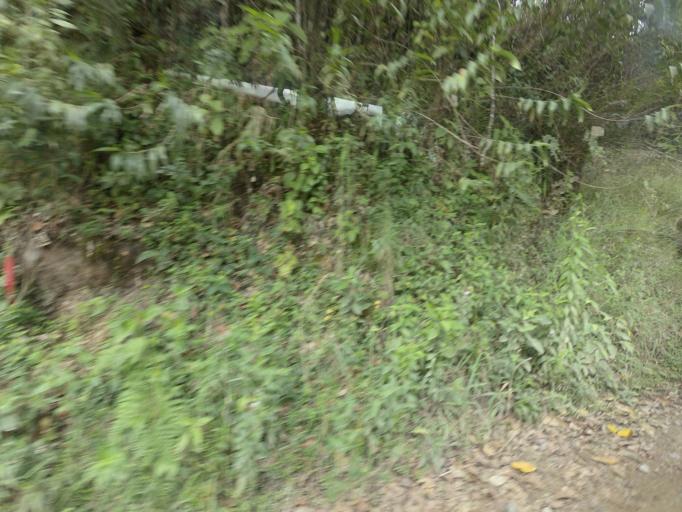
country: CO
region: Huila
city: San Agustin
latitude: 1.9291
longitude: -76.3013
